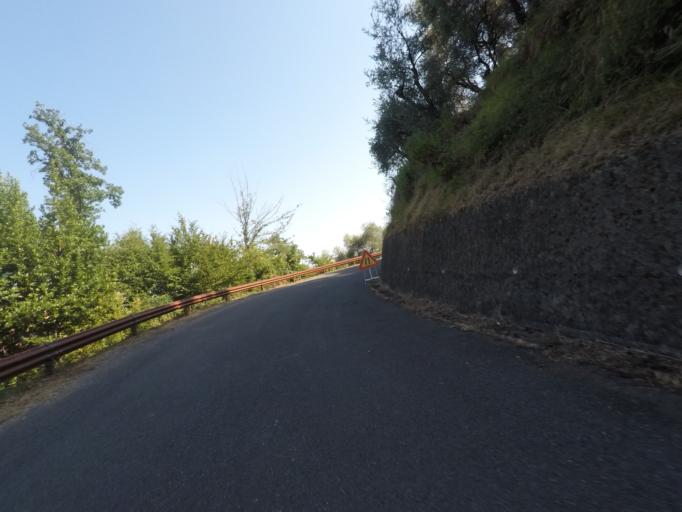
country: IT
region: Tuscany
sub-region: Provincia di Massa-Carrara
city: Carrara
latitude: 44.0752
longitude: 10.0711
